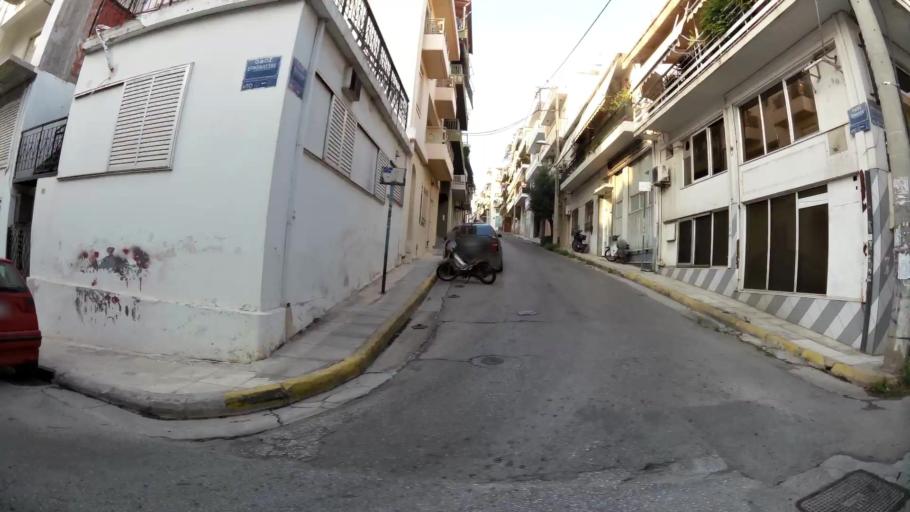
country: GR
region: Attica
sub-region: Nomarchia Athinas
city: Galatsi
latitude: 38.0275
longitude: 23.7469
